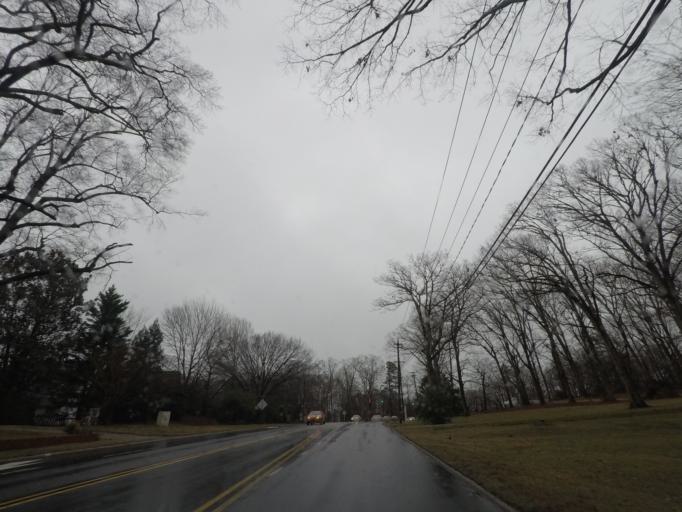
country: US
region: North Carolina
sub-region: Durham County
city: Durham
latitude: 36.0412
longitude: -78.9590
